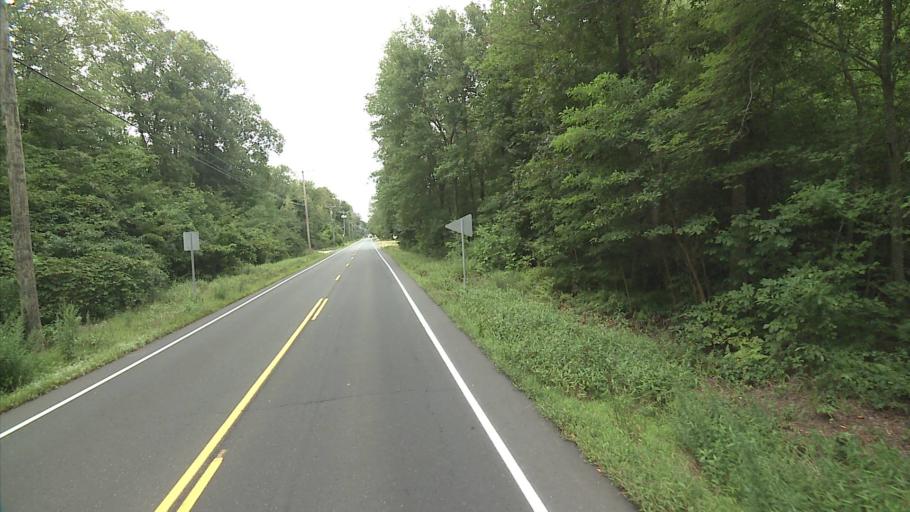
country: US
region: Connecticut
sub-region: New London County
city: Colchester
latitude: 41.5424
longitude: -72.3052
